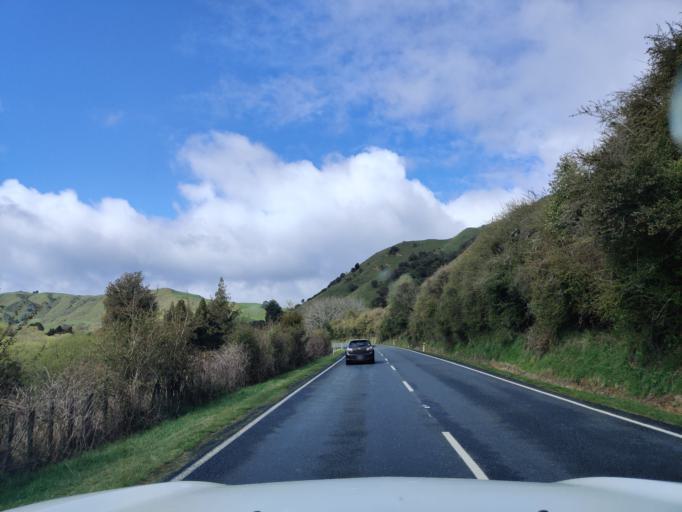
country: NZ
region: Waikato
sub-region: Otorohanga District
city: Otorohanga
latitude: -38.5895
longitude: 175.2176
